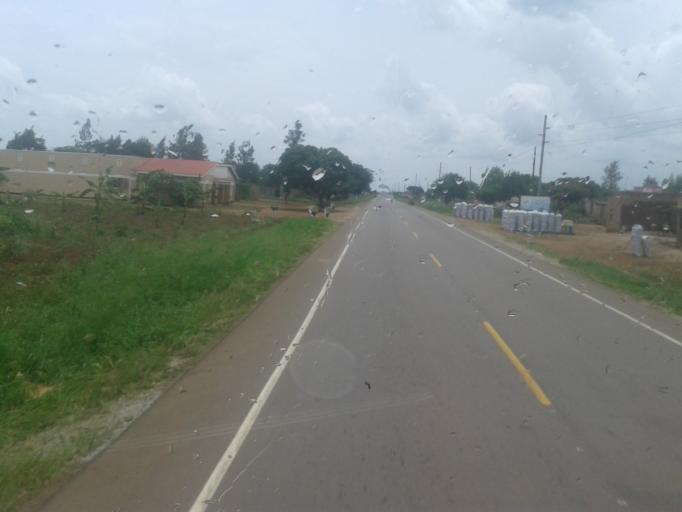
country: UG
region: Western Region
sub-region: Kiryandongo District
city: Masindi Port
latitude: 1.7593
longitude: 32.0209
